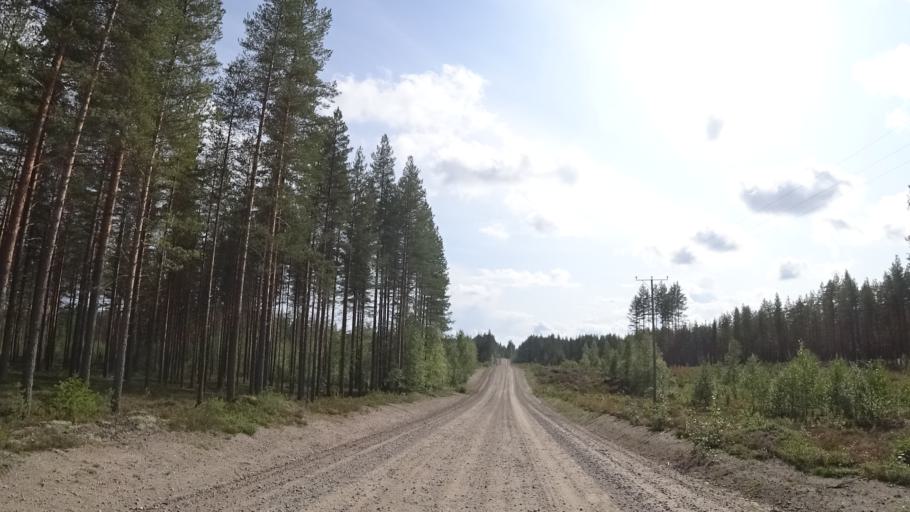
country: FI
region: North Karelia
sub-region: Pielisen Karjala
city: Lieksa
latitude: 63.5613
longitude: 30.0680
